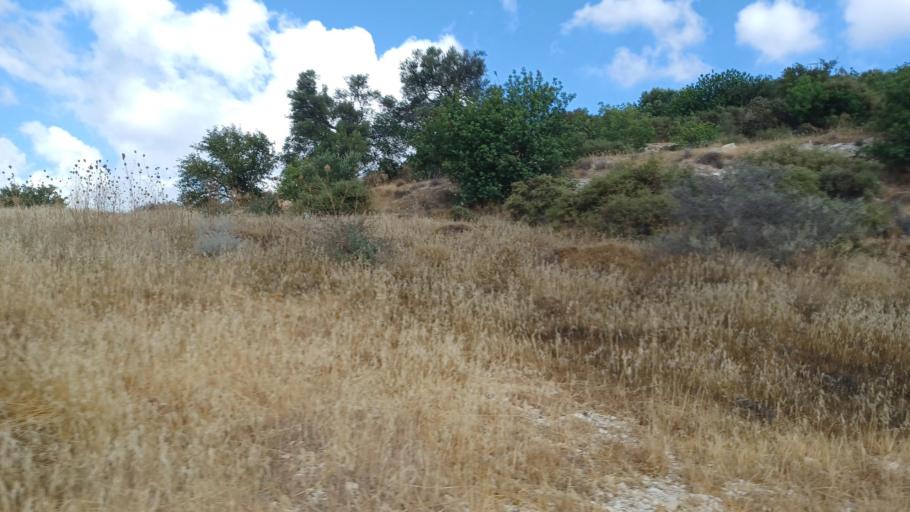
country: CY
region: Limassol
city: Pachna
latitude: 34.8012
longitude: 32.6657
